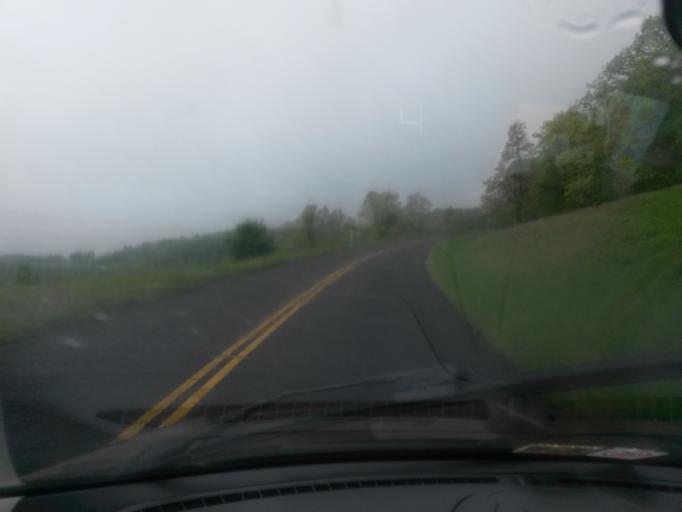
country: US
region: Virginia
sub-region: Floyd County
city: Floyd
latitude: 36.7993
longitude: -80.3816
